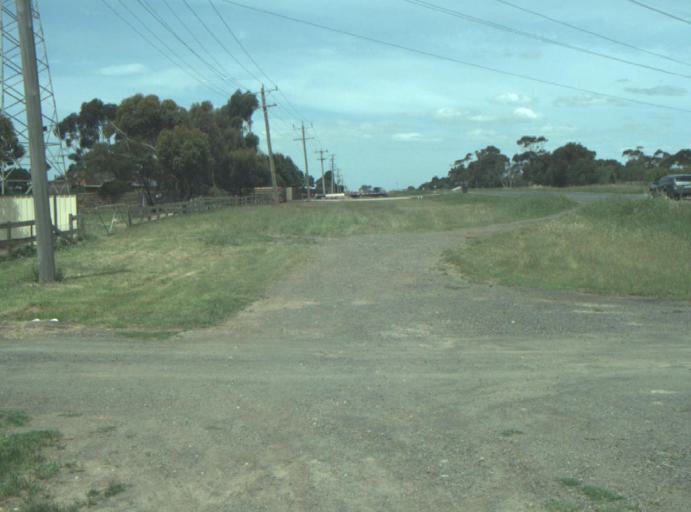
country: AU
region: Victoria
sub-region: Greater Geelong
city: Lara
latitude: -38.0342
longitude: 144.3554
